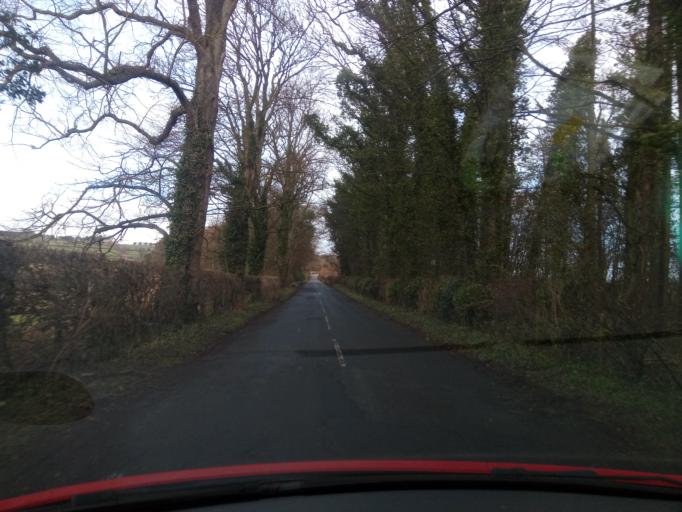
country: GB
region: England
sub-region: Northumberland
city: Corbridge
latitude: 54.9835
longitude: -2.0408
